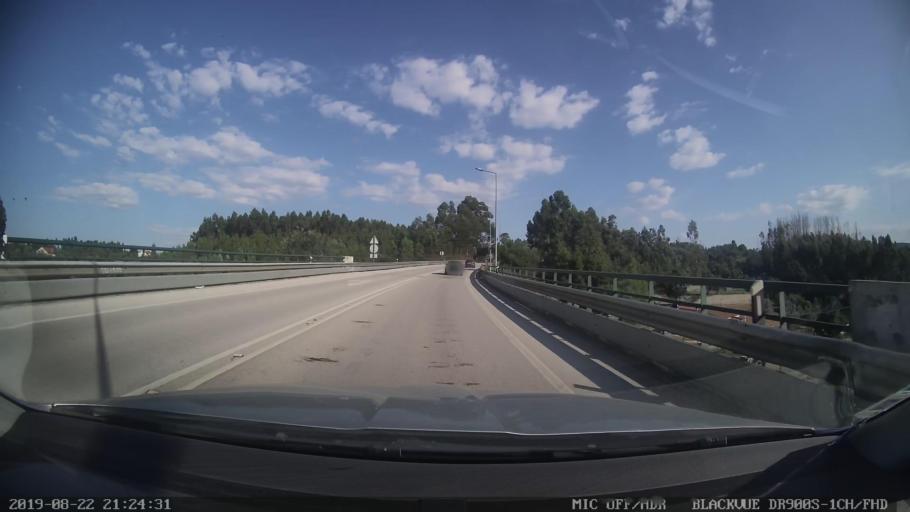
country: PT
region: Castelo Branco
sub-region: Serta
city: Serta
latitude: 39.8421
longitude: -8.1236
